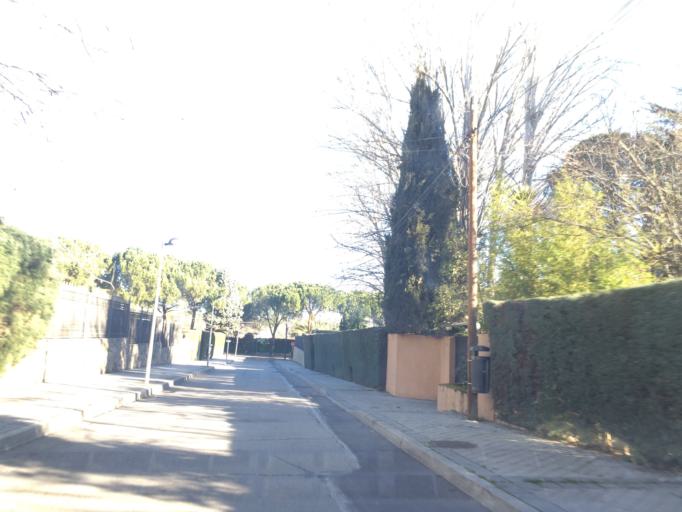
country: ES
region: Madrid
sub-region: Provincia de Madrid
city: Tres Cantos
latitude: 40.6113
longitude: -3.6869
